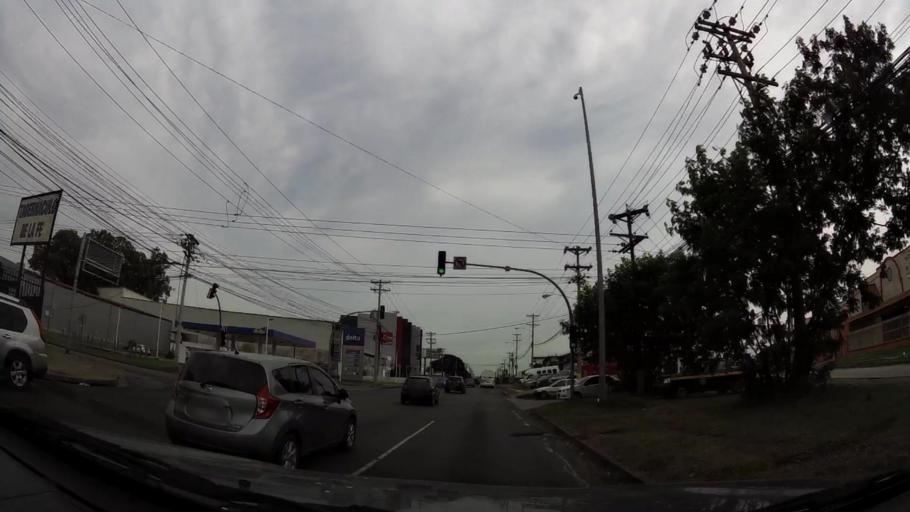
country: PA
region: Panama
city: San Miguelito
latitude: 9.0388
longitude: -79.4637
